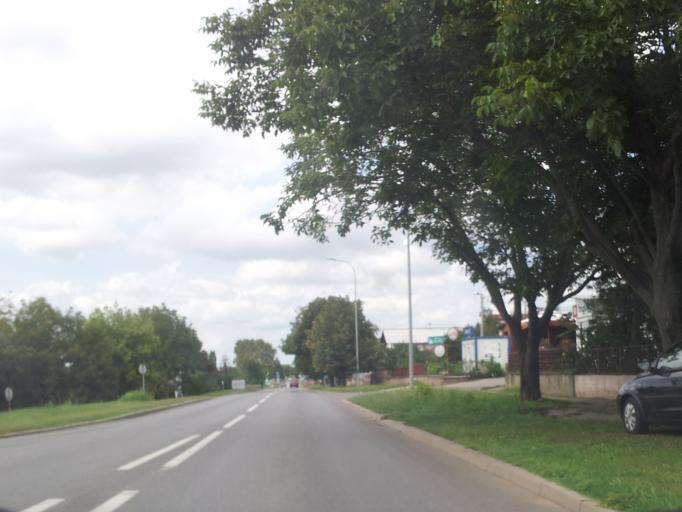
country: HR
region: Osjecko-Baranjska
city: Beli Manastir
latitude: 45.7640
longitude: 18.6224
